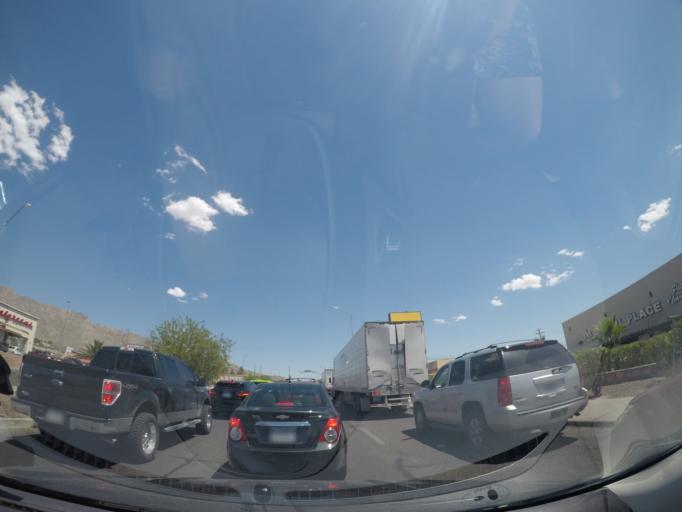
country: US
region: New Mexico
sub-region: Dona Ana County
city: Sunland Park
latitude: 31.8292
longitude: -106.5284
